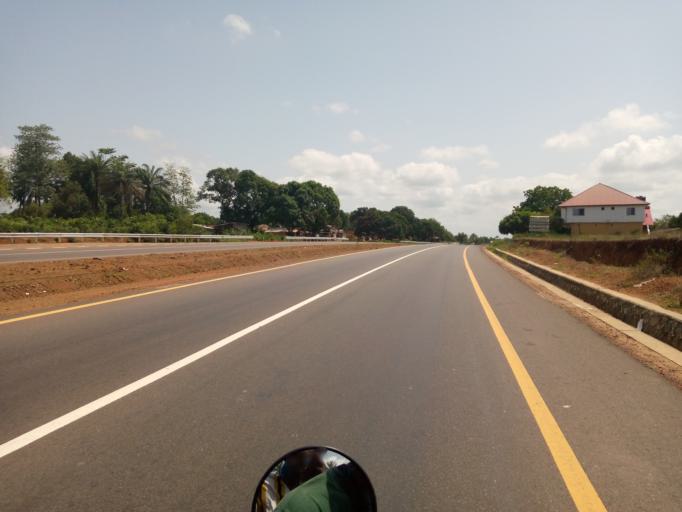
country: SL
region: Western Area
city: Waterloo
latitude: 8.3785
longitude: -12.9582
